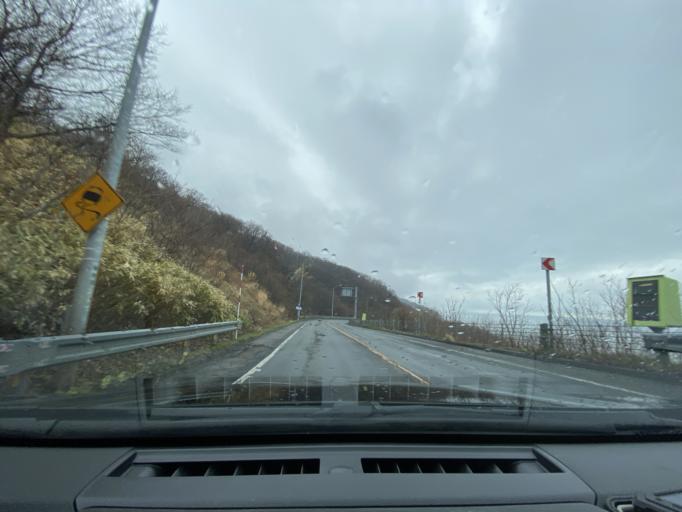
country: JP
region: Hokkaido
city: Rumoi
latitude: 43.8178
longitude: 141.4231
